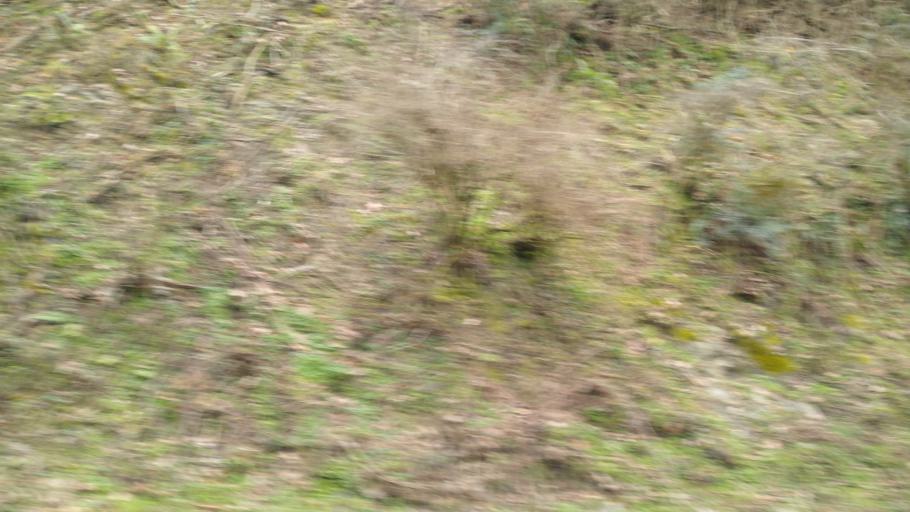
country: JP
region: Kyoto
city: Ayabe
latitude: 35.3375
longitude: 135.3467
